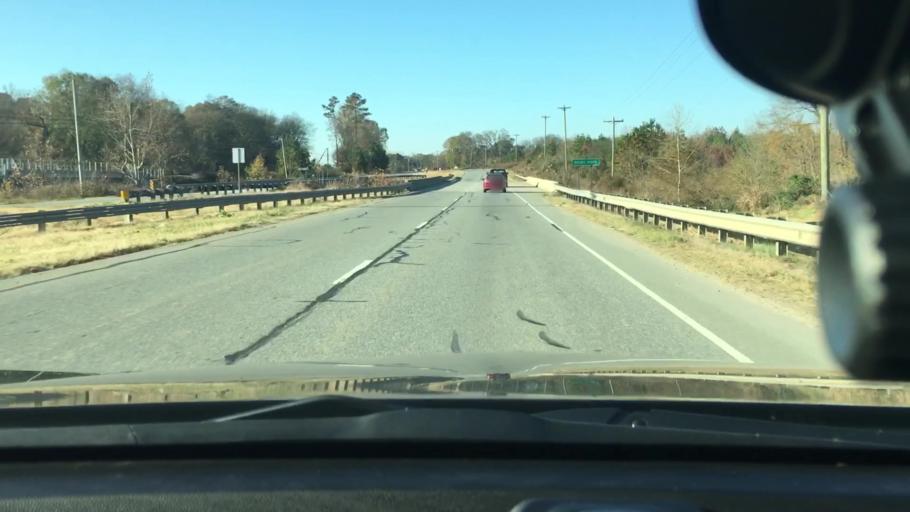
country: US
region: North Carolina
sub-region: Cabarrus County
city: Harrisburg
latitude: 35.3331
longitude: -80.6273
